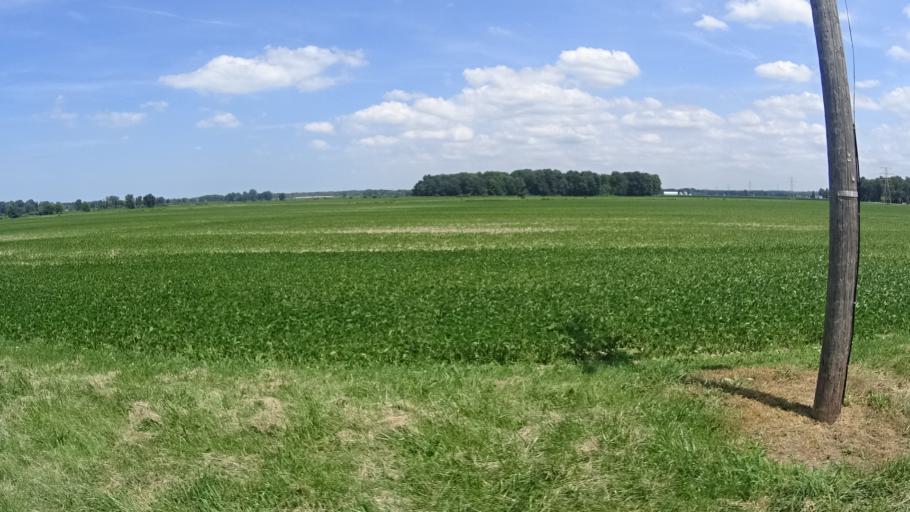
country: US
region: Ohio
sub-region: Erie County
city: Huron
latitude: 41.3597
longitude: -82.5376
